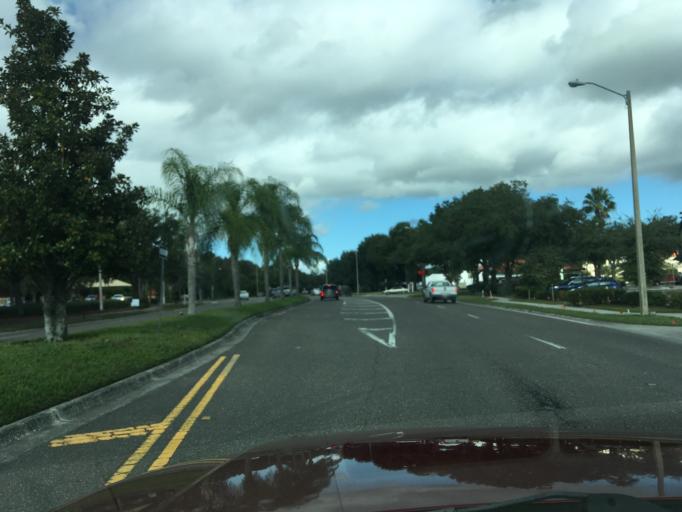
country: US
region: Florida
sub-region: Hillsborough County
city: Sun City Center
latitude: 27.7135
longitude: -82.3769
